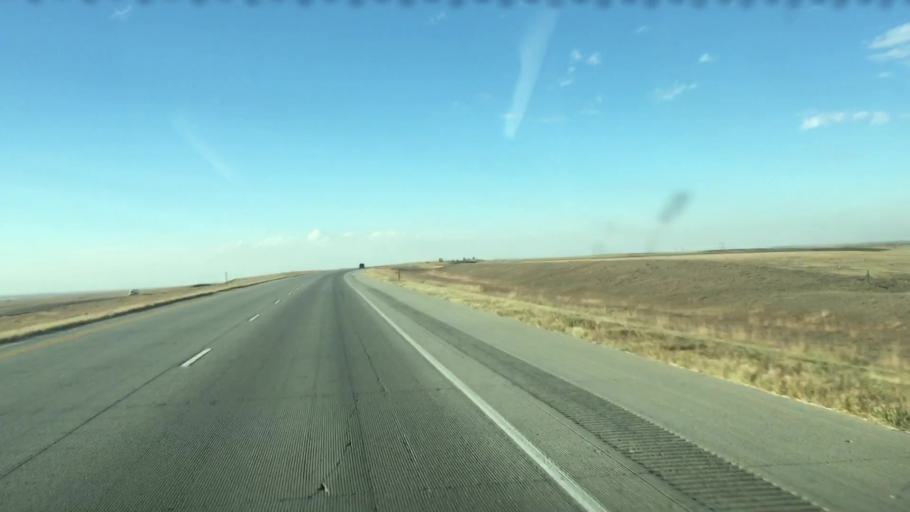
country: US
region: Colorado
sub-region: Lincoln County
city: Limon
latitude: 39.3759
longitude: -103.8842
